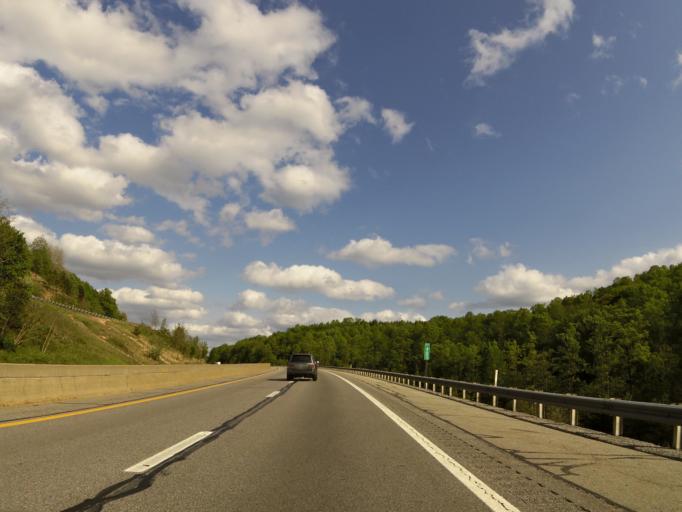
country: US
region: West Virginia
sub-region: Raleigh County
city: MacArthur
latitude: 37.7333
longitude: -81.2045
